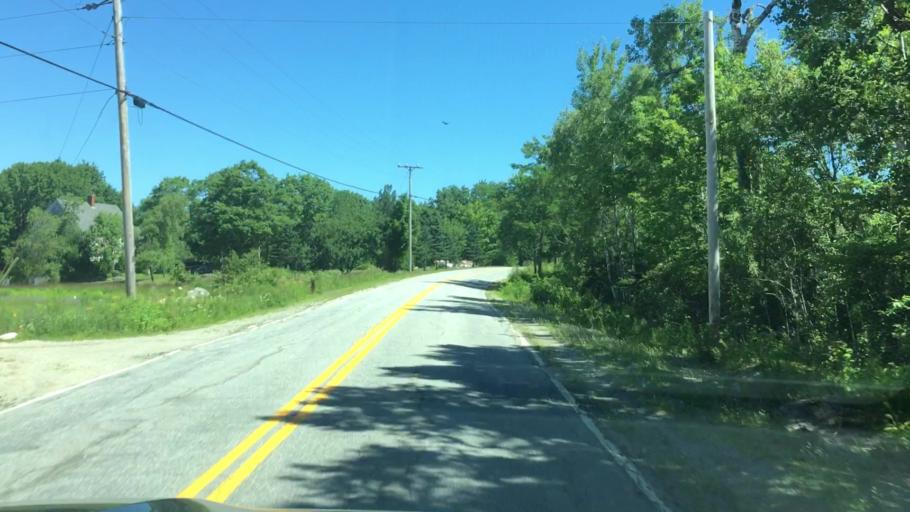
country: US
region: Maine
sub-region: Hancock County
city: Penobscot
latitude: 44.5163
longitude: -68.6703
